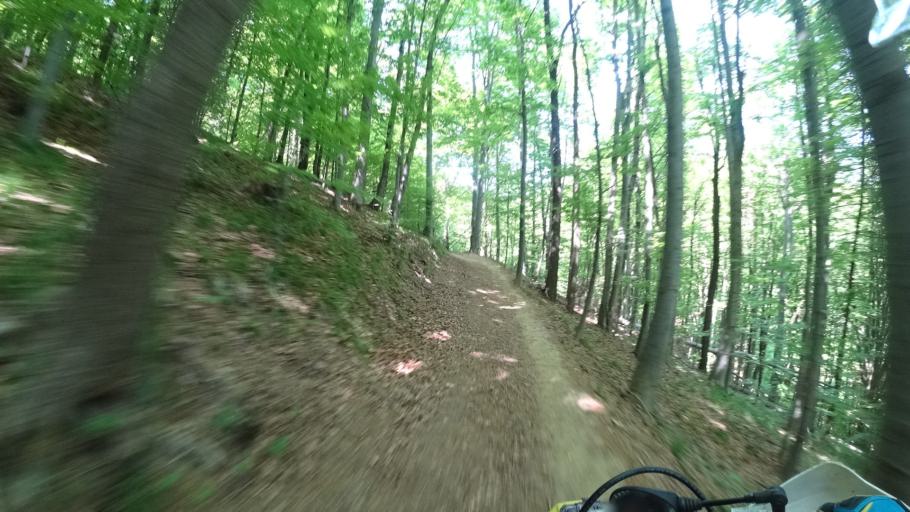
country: HR
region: Zagrebacka
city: Jablanovec
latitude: 45.8770
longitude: 15.8967
